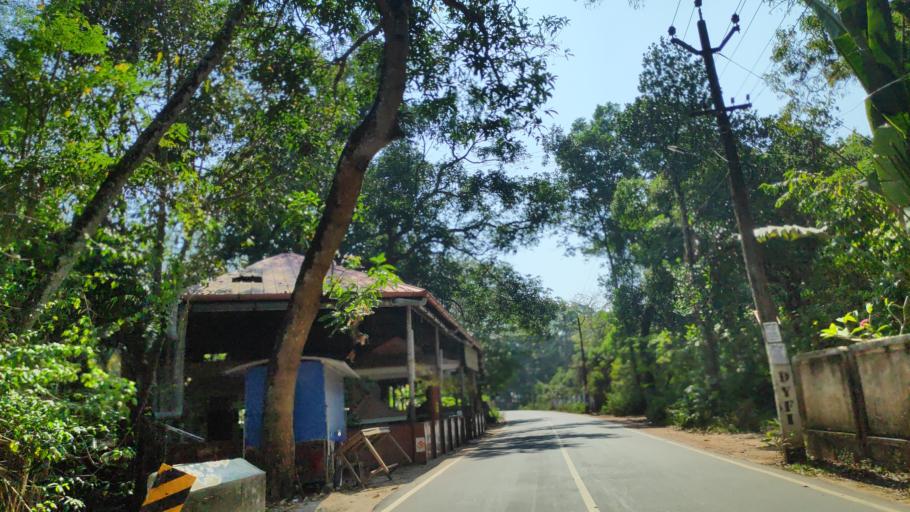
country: IN
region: Kerala
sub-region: Alappuzha
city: Shertallai
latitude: 9.6413
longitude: 76.3164
